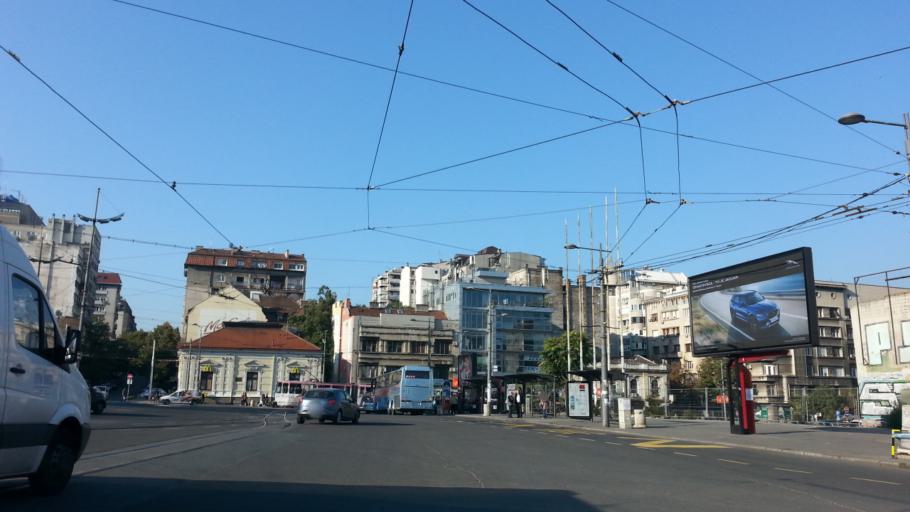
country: RS
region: Central Serbia
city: Belgrade
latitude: 44.8030
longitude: 20.4664
